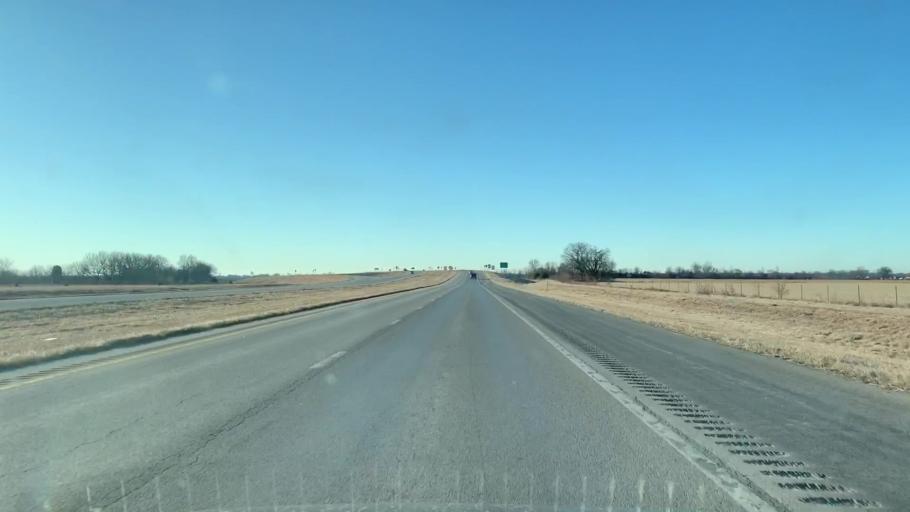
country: US
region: Kansas
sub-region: Bourbon County
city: Fort Scott
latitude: 37.7755
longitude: -94.7058
